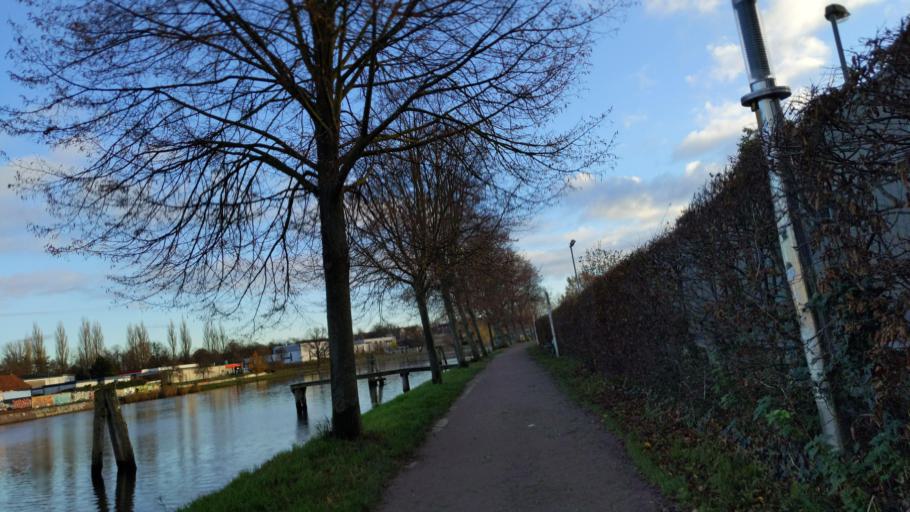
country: DE
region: Schleswig-Holstein
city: Luebeck
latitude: 53.8722
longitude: 10.6944
